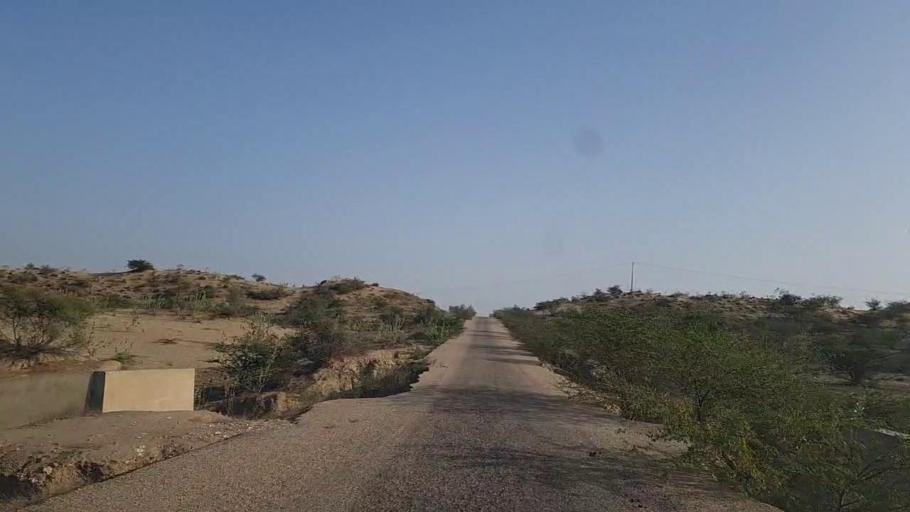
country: PK
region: Sindh
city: Diplo
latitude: 24.6087
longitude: 69.3776
